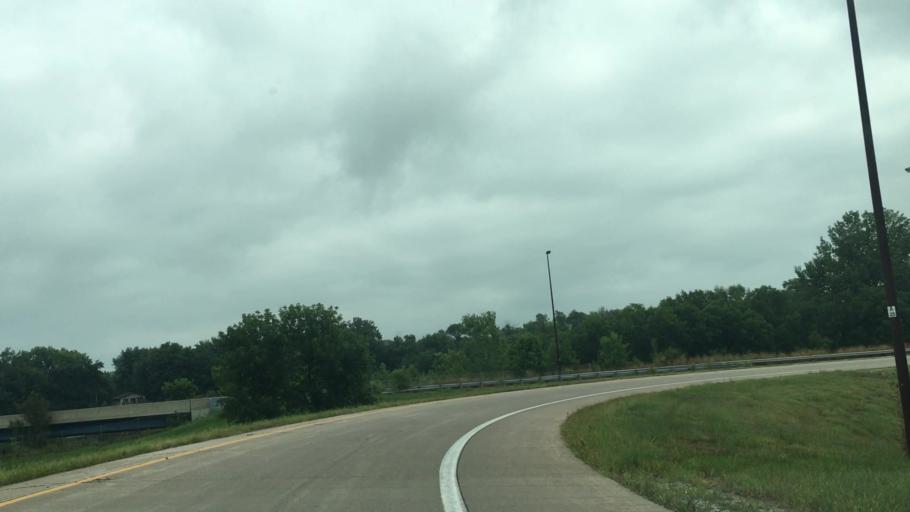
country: US
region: Illinois
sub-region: Rock Island County
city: Coal Valley
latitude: 41.4592
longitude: -90.4948
